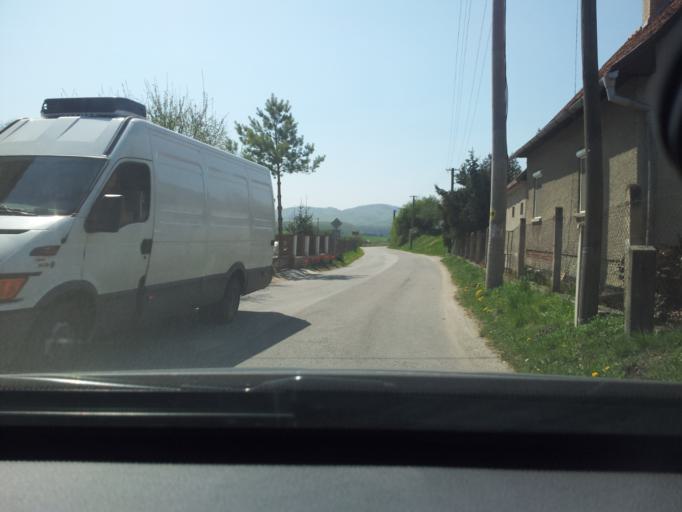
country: SK
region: Nitriansky
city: Partizanske
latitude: 48.5808
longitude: 18.3208
